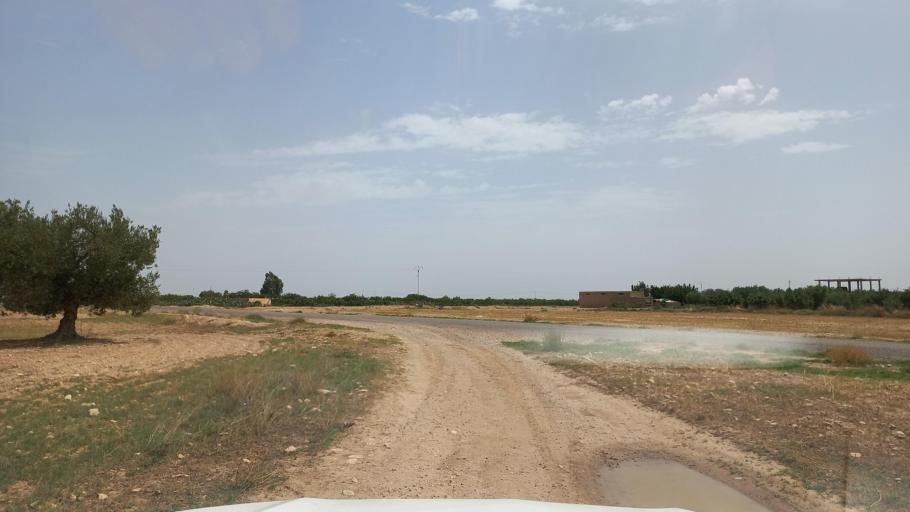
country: TN
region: Al Qasrayn
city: Kasserine
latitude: 35.2871
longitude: 9.0334
